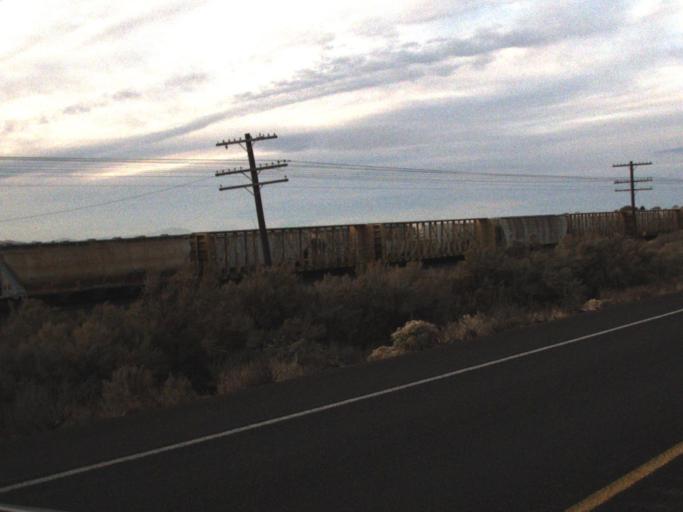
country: US
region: Washington
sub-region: Benton County
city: Finley
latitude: 46.0893
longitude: -118.9106
